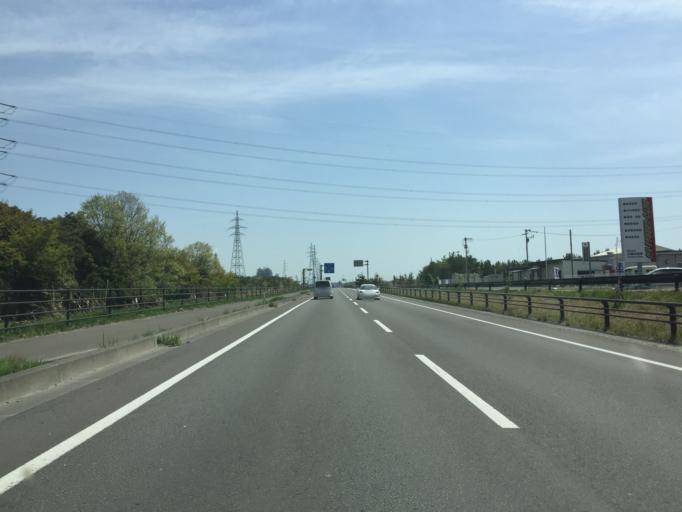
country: JP
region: Miyagi
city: Marumori
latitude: 37.8420
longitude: 140.9366
